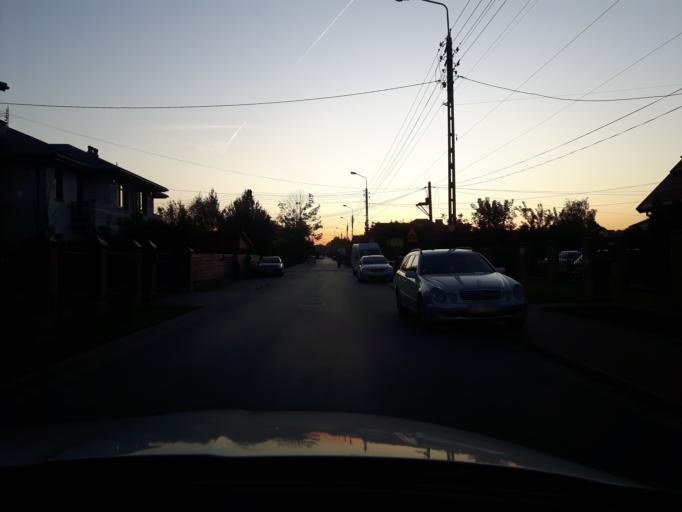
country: PL
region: Masovian Voivodeship
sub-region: Powiat wolominski
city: Kobylka
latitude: 52.3375
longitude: 21.1901
